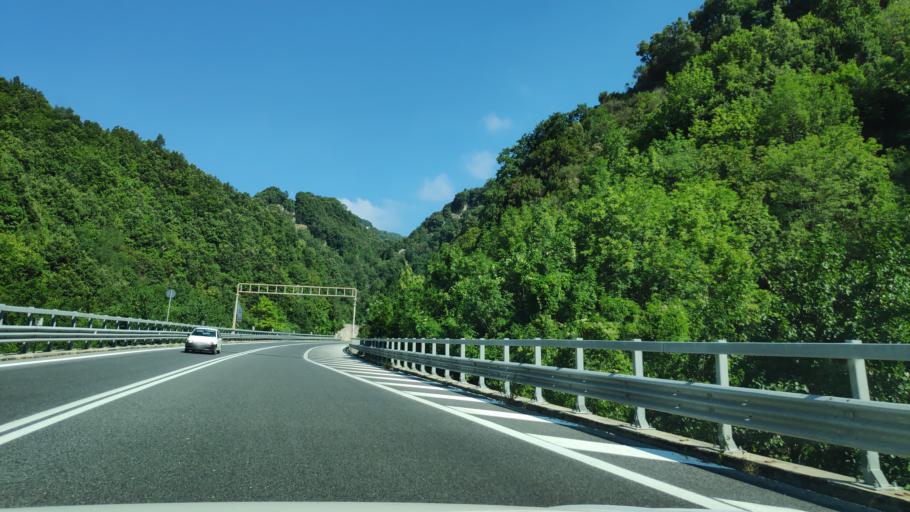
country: IT
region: Calabria
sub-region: Provincia di Reggio Calabria
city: Amato
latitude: 38.3729
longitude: 16.1794
